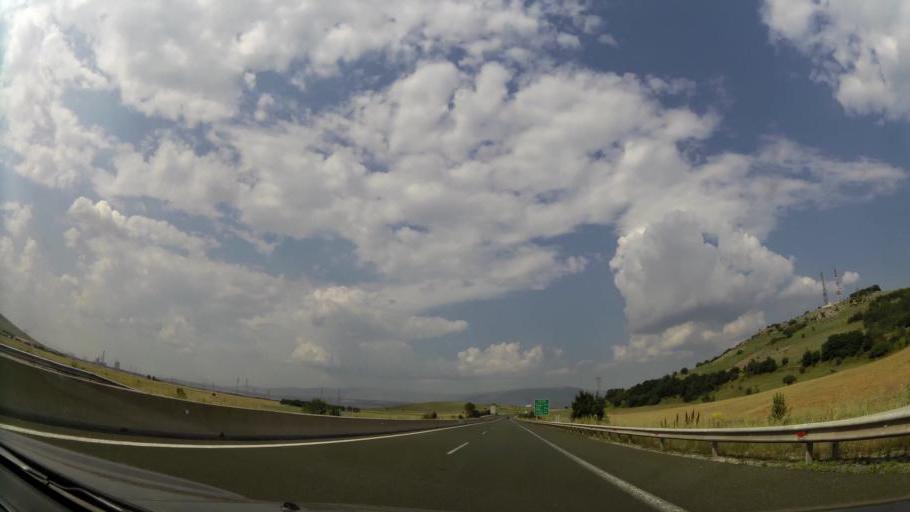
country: GR
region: West Macedonia
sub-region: Nomos Kozanis
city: Koila
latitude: 40.3552
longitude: 21.8128
